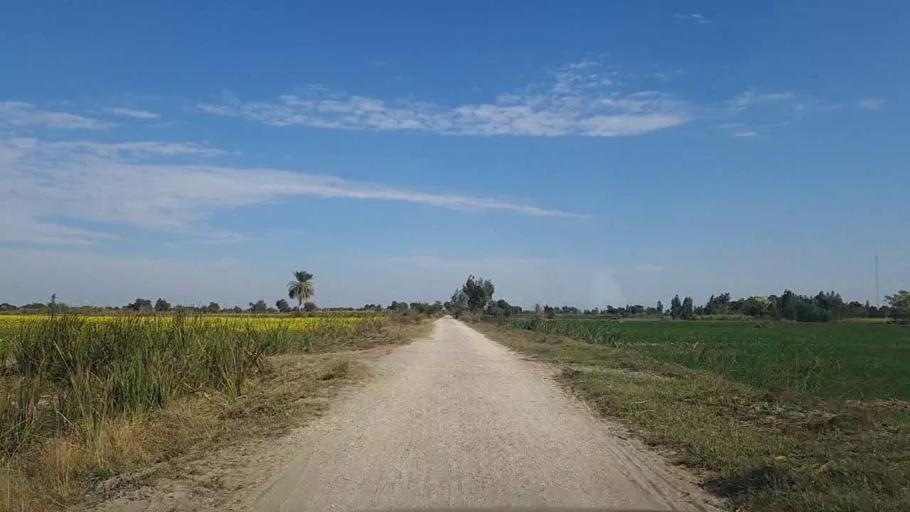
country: PK
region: Sindh
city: Khadro
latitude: 26.2733
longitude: 68.8117
